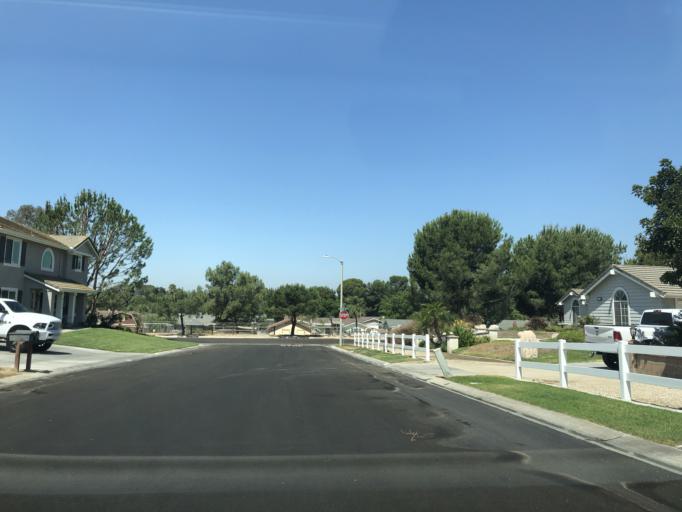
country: US
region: California
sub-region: Riverside County
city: Norco
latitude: 33.9203
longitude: -117.5758
